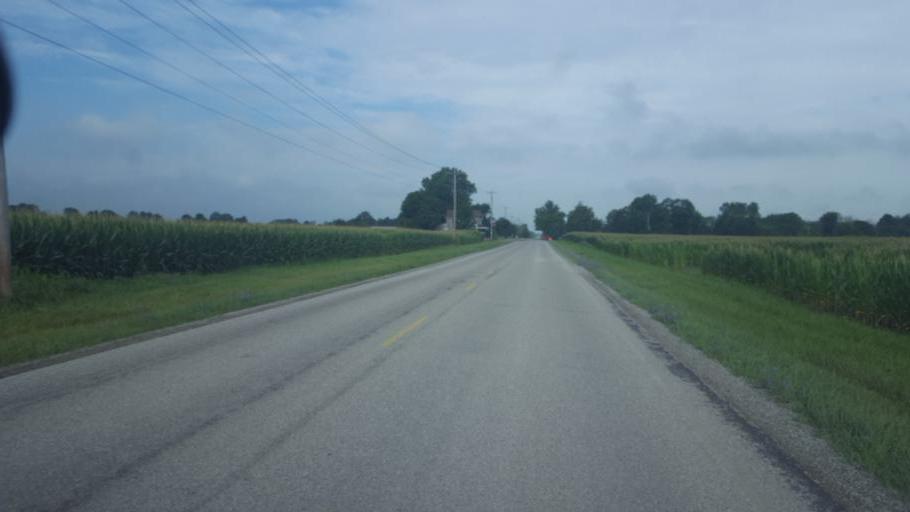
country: US
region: Ohio
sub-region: Delaware County
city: Ashley
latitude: 40.4069
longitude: -82.8963
